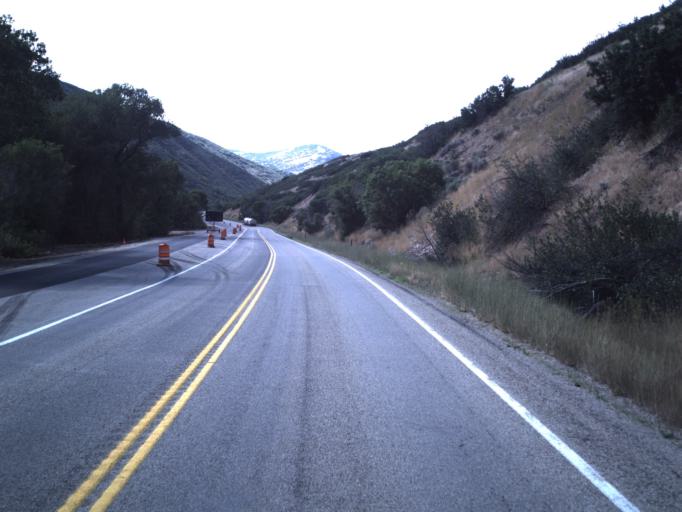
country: US
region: Utah
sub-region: Wasatch County
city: Heber
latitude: 40.4198
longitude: -111.3363
